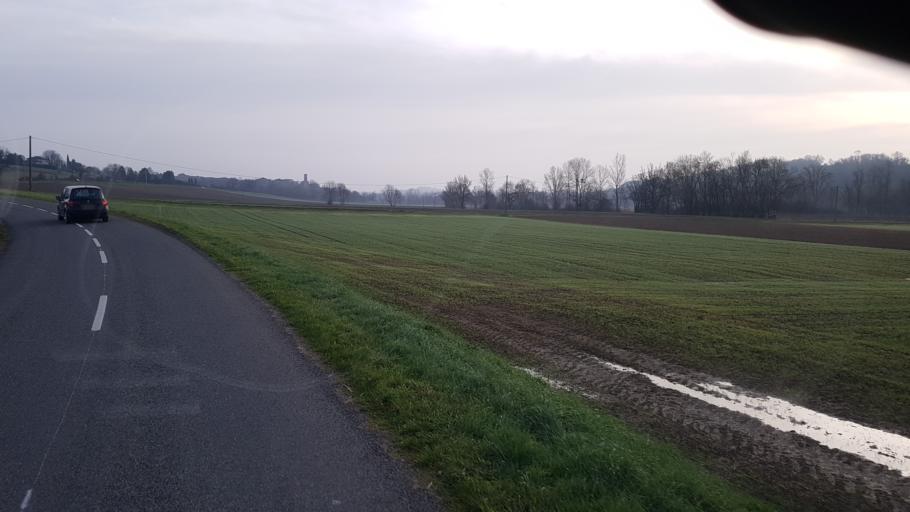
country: FR
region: Midi-Pyrenees
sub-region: Departement du Tarn
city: Cahuzac-sur-Vere
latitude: 43.9873
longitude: 1.8260
